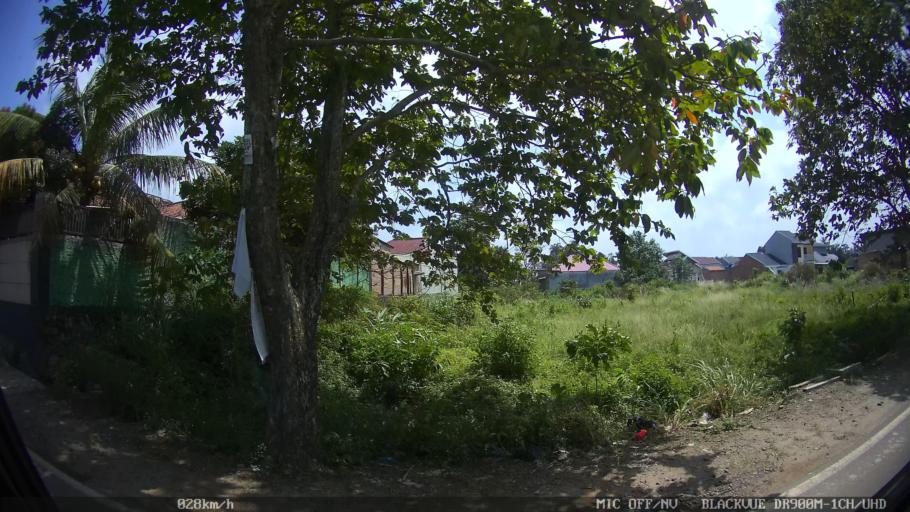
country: ID
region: Lampung
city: Kedaton
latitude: -5.3506
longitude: 105.2869
